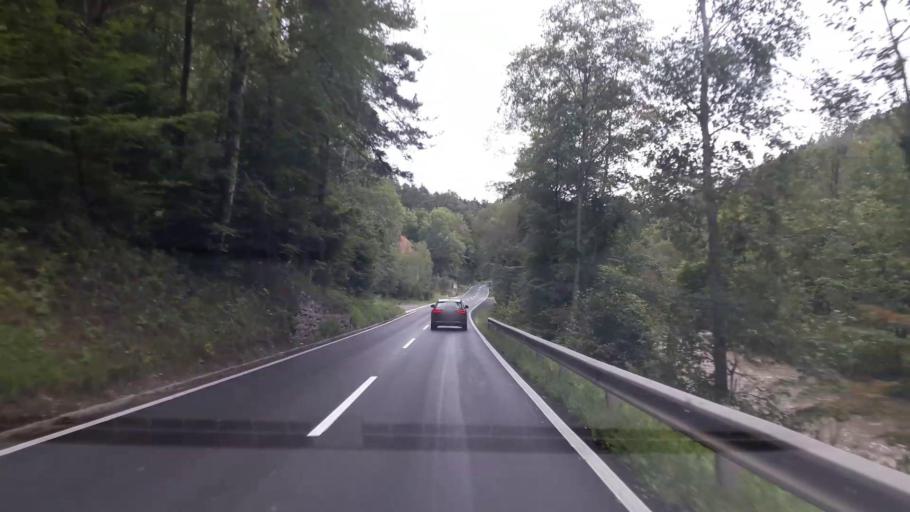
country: AT
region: Styria
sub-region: Politischer Bezirk Hartberg-Fuerstenfeld
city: Stubenberg
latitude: 47.2437
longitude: 15.7870
